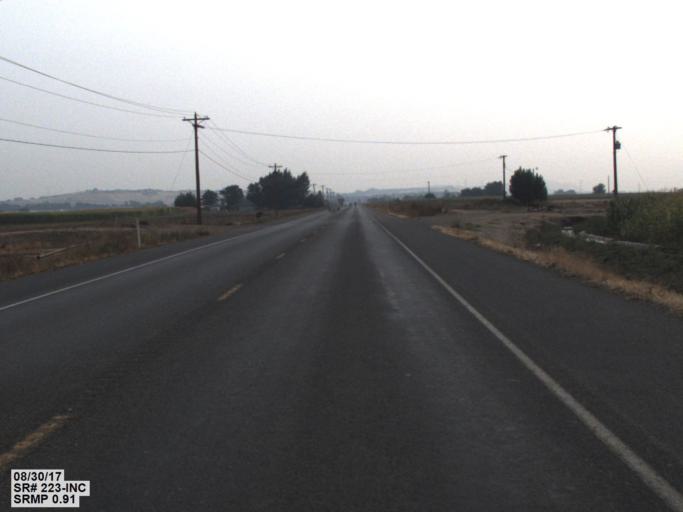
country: US
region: Washington
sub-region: Yakima County
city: Granger
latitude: 46.3284
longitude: -120.2272
